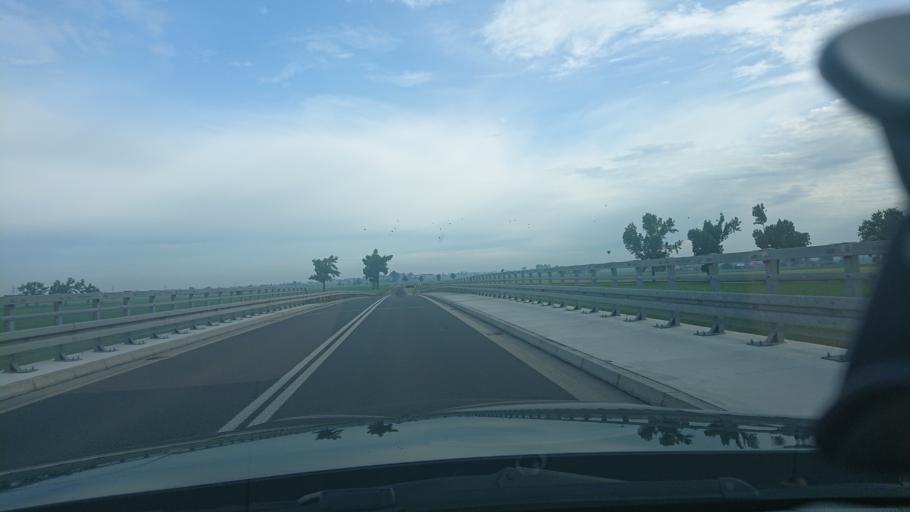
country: PL
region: Greater Poland Voivodeship
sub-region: Powiat gnieznienski
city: Gniezno
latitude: 52.5683
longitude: 17.5714
